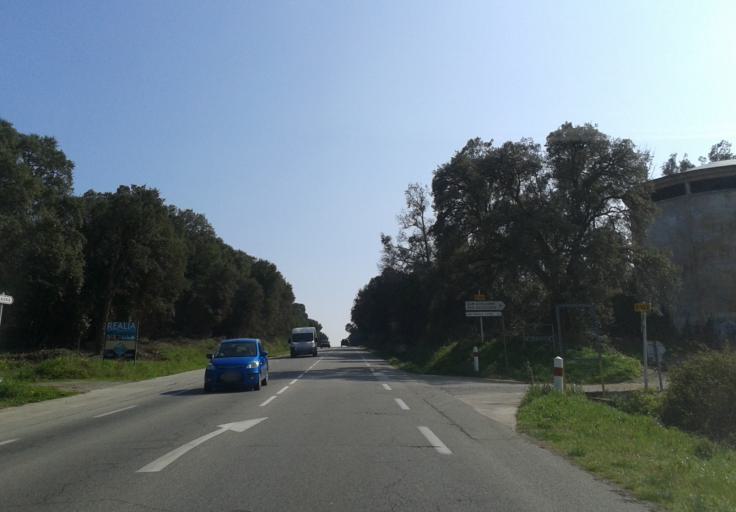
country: FR
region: Corsica
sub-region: Departement de la Haute-Corse
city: Cervione
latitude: 42.3049
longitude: 9.5437
